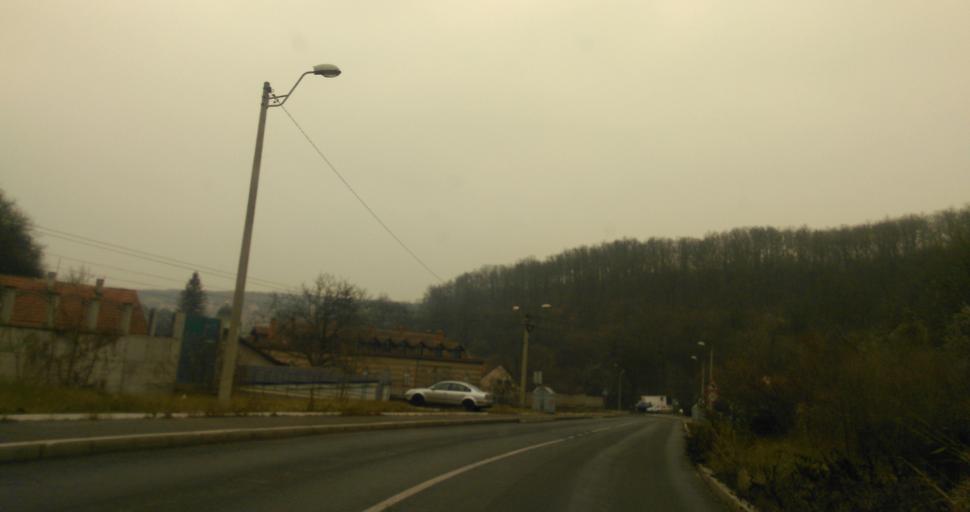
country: RS
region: Central Serbia
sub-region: Belgrade
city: Rakovica
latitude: 44.7294
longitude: 20.4467
